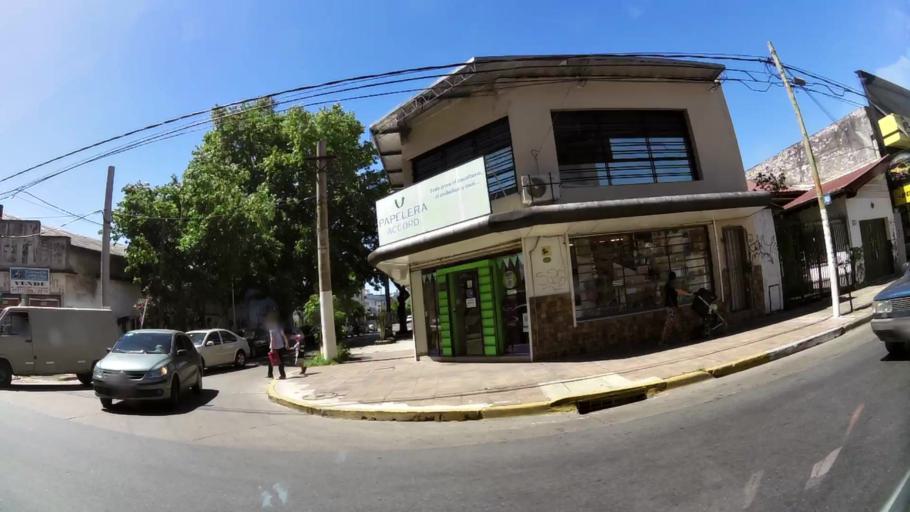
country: AR
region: Buenos Aires
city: Caseros
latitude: -34.6009
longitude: -58.5472
